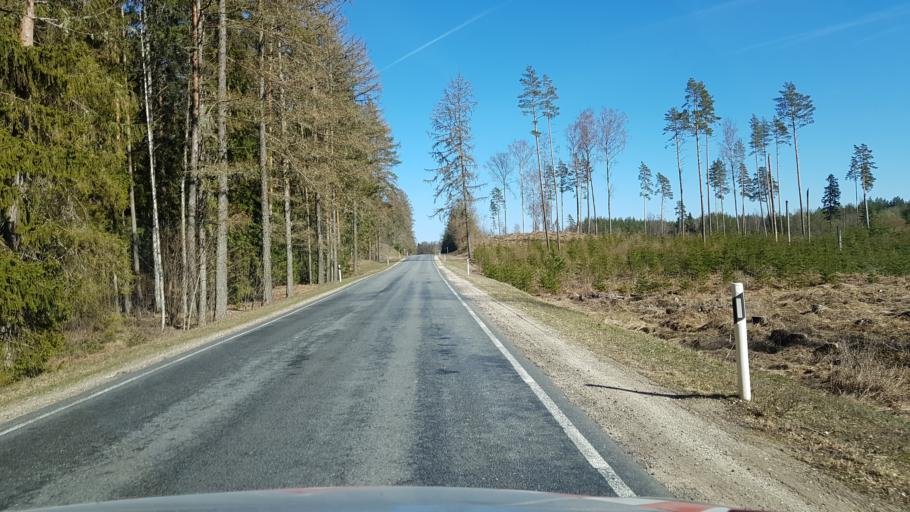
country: EE
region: Laeaene-Virumaa
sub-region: Vinni vald
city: Vinni
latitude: 59.2731
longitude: 26.6355
